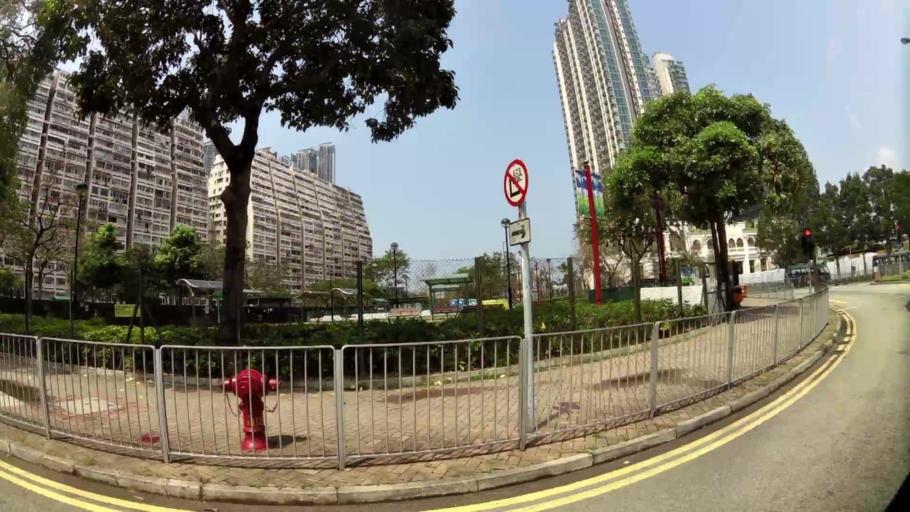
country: HK
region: Kowloon City
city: Kowloon
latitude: 22.3087
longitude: 114.1676
